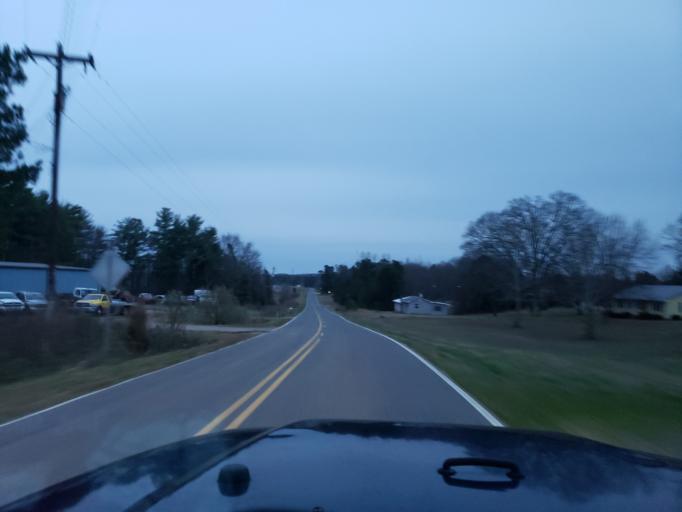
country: US
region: North Carolina
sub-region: Cleveland County
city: White Plains
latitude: 35.1770
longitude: -81.4134
